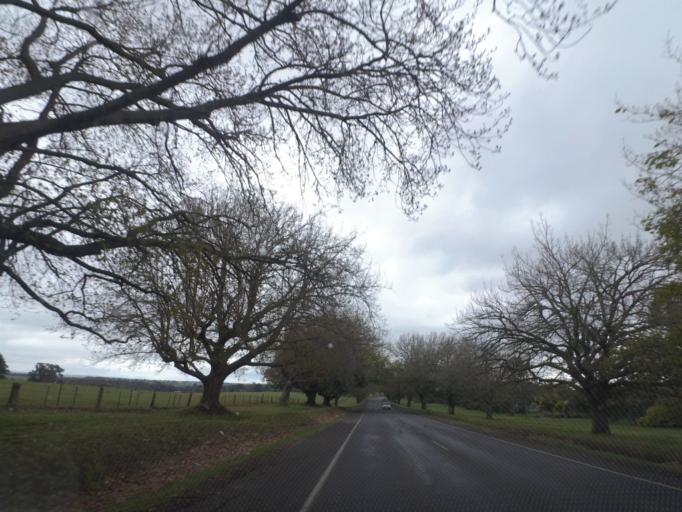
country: AU
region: Victoria
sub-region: Hume
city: Sunbury
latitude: -37.3401
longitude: 144.5277
